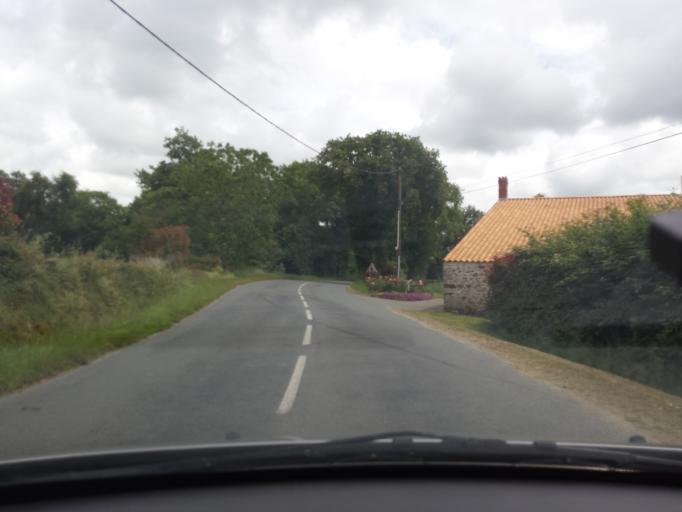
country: FR
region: Pays de la Loire
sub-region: Departement de la Vendee
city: Beaulieu-sous-la-Roche
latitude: 46.6711
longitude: -1.5993
